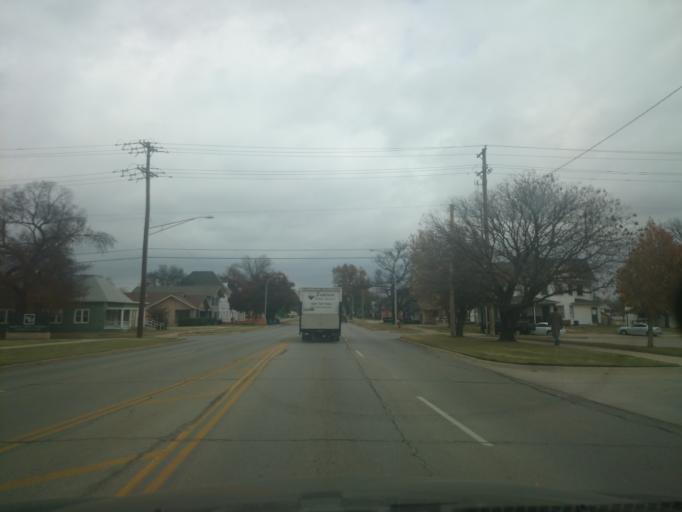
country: US
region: Oklahoma
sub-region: Payne County
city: Stillwater
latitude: 36.1162
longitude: -97.0627
